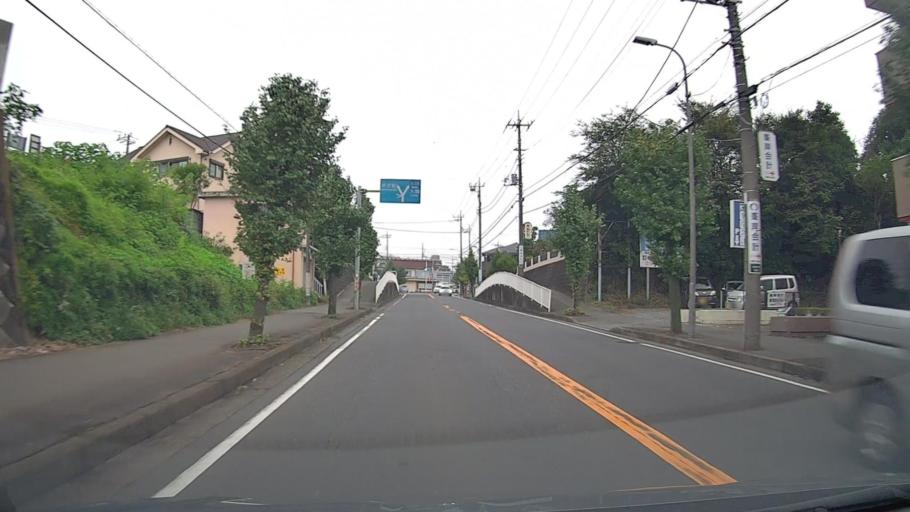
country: JP
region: Saitama
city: Tokorozawa
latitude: 35.7805
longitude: 139.4781
